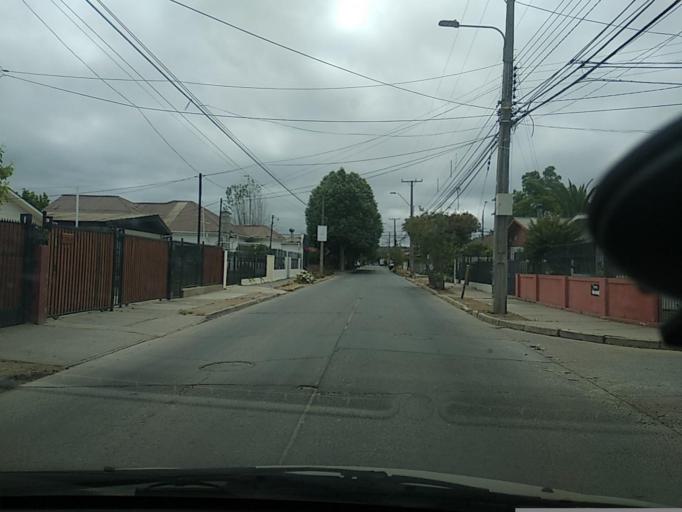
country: CL
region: Valparaiso
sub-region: Provincia de Marga Marga
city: Villa Alemana
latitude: -33.0406
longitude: -71.3687
